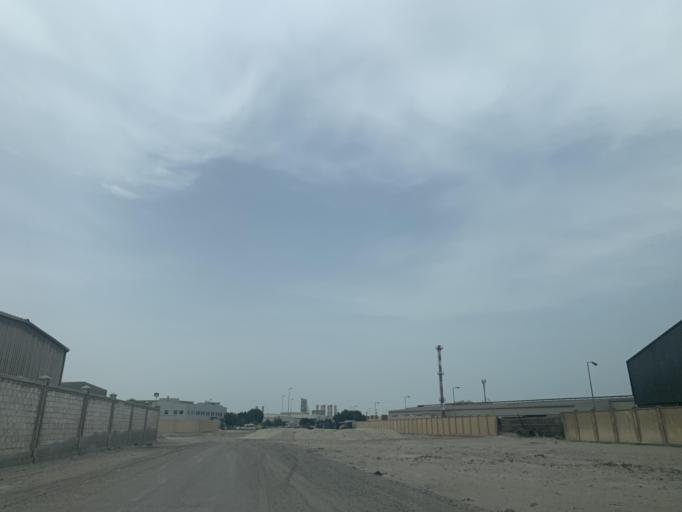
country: BH
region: Muharraq
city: Al Hadd
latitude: 26.2083
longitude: 50.6685
